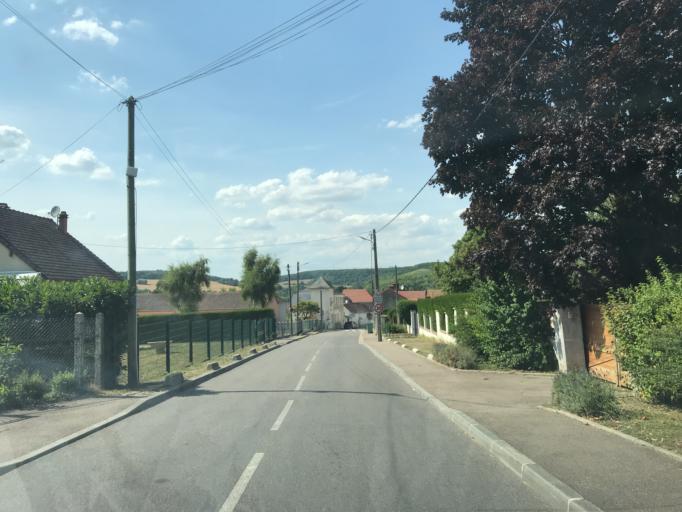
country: FR
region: Haute-Normandie
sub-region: Departement de l'Eure
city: Gasny
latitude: 49.0744
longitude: 1.5954
